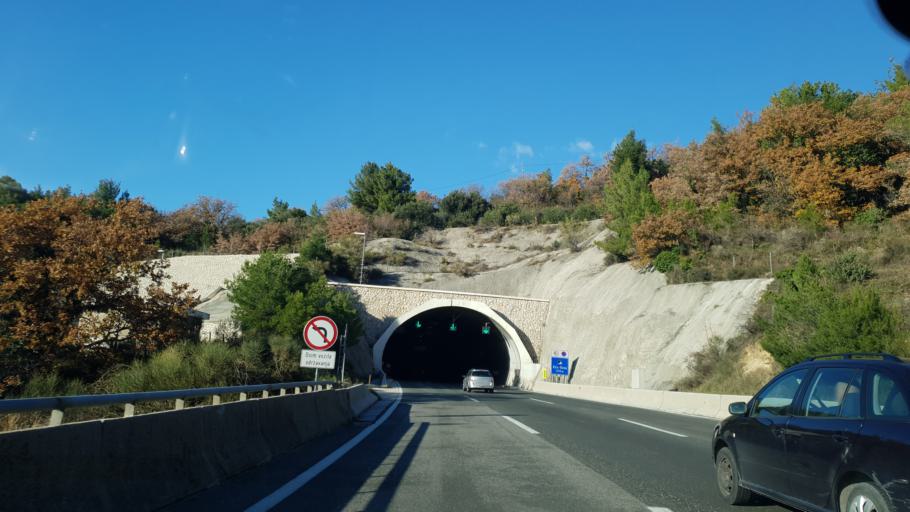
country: HR
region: Splitsko-Dalmatinska
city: Klis
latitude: 43.5484
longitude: 16.5354
